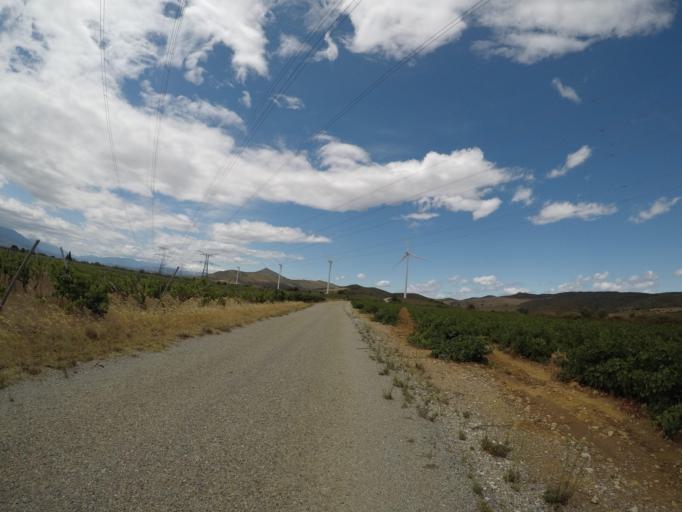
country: FR
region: Languedoc-Roussillon
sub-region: Departement des Pyrenees-Orientales
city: Pezilla-la-Riviere
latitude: 42.7212
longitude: 2.7553
